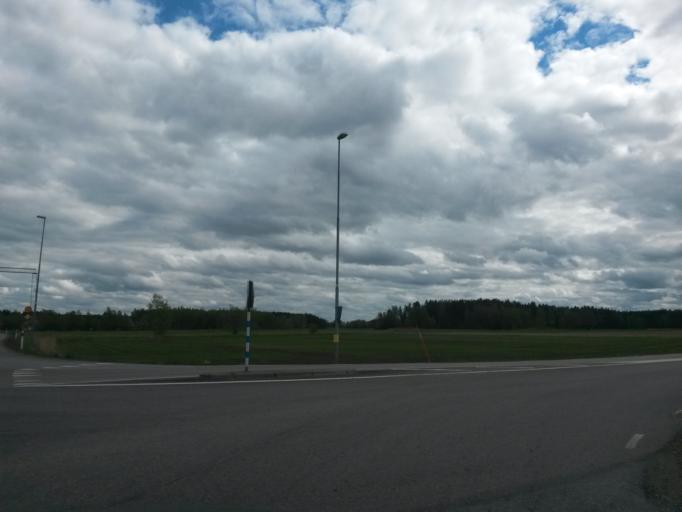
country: SE
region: Vaestra Goetaland
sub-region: Grastorps Kommun
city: Graestorp
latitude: 58.3304
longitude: 12.6907
